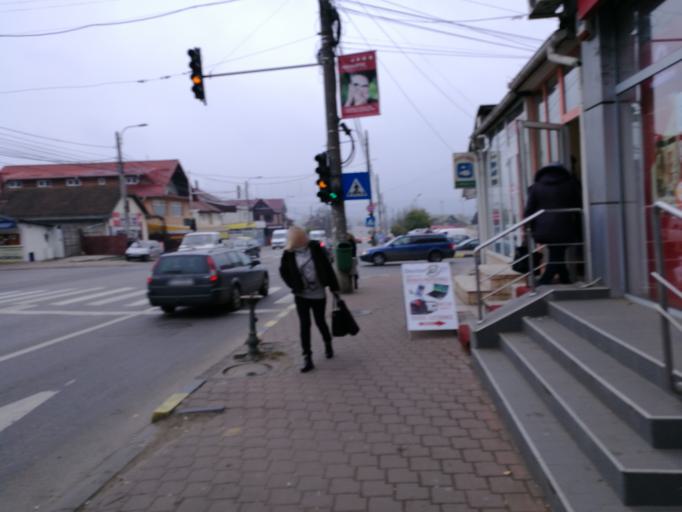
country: RO
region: Suceava
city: Suceava
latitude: 47.6710
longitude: 26.2774
